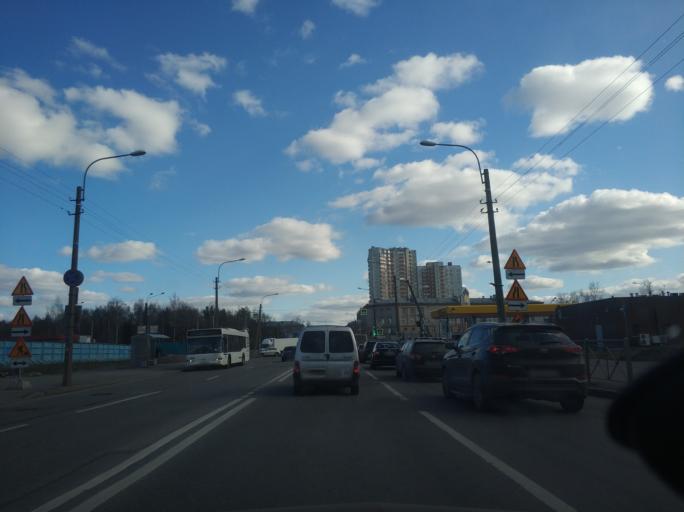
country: RU
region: St.-Petersburg
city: Krasnogvargeisky
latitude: 59.9628
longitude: 30.4876
